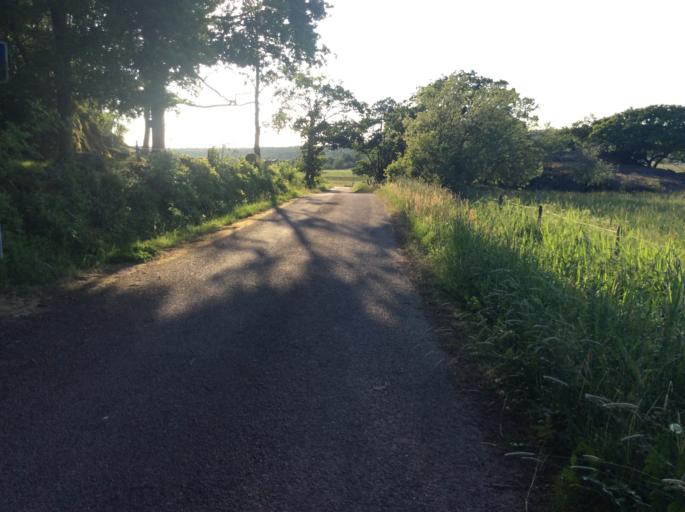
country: SE
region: Vaestra Goetaland
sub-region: Goteborg
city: Torslanda
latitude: 57.7967
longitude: 11.8606
